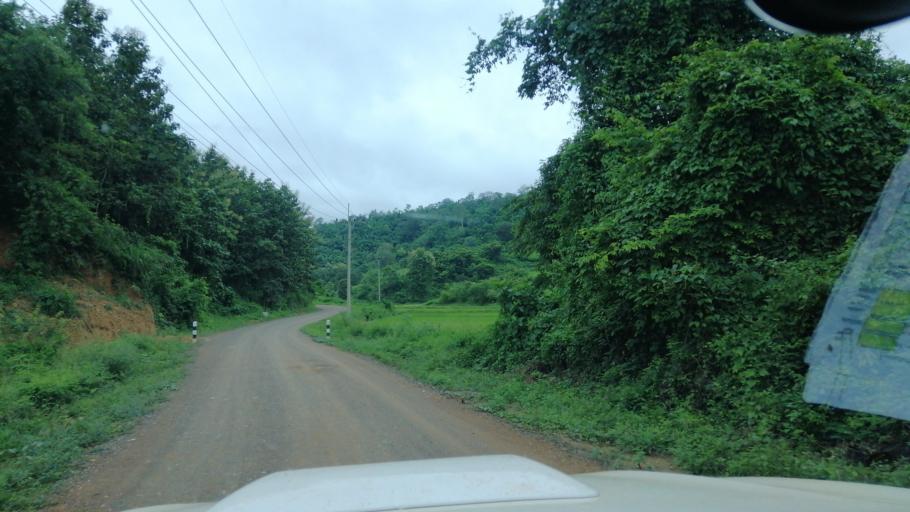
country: LA
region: Xiagnabouli
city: Muang Kenthao
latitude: 17.9433
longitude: 101.3954
